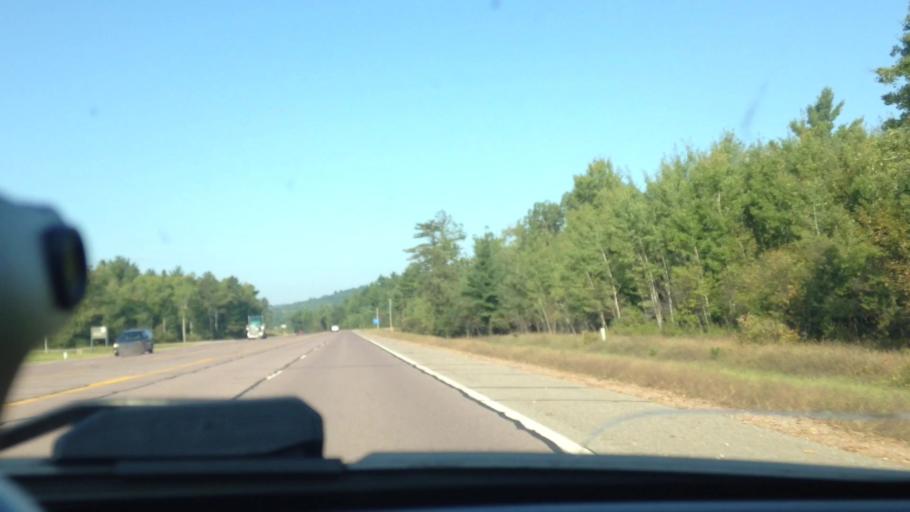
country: US
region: Michigan
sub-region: Dickinson County
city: Quinnesec
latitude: 45.8032
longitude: -87.9641
